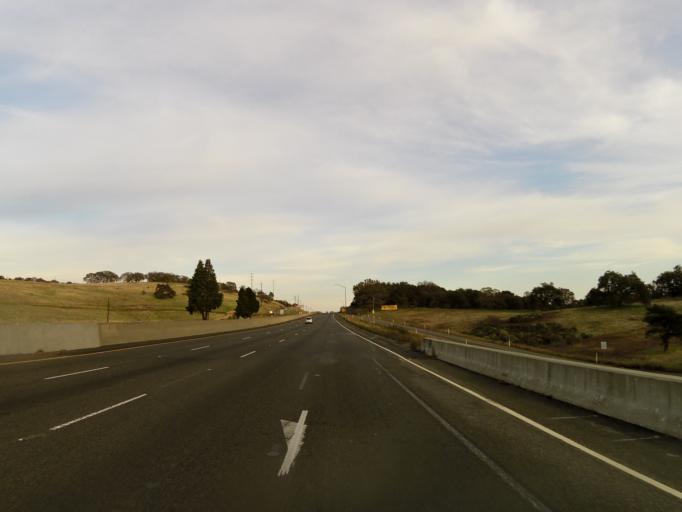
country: US
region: California
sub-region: El Dorado County
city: Cameron Park
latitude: 38.6552
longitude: -121.0300
